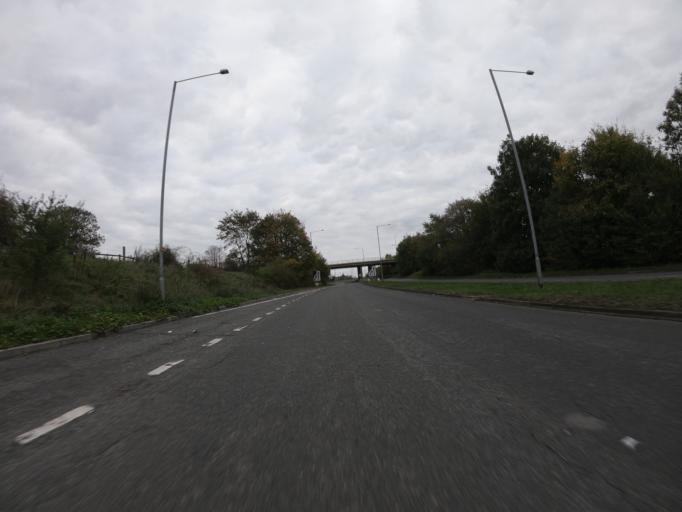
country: GB
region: England
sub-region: Borough of Thurrock
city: Chadwell St Mary
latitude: 51.4838
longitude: 0.3482
